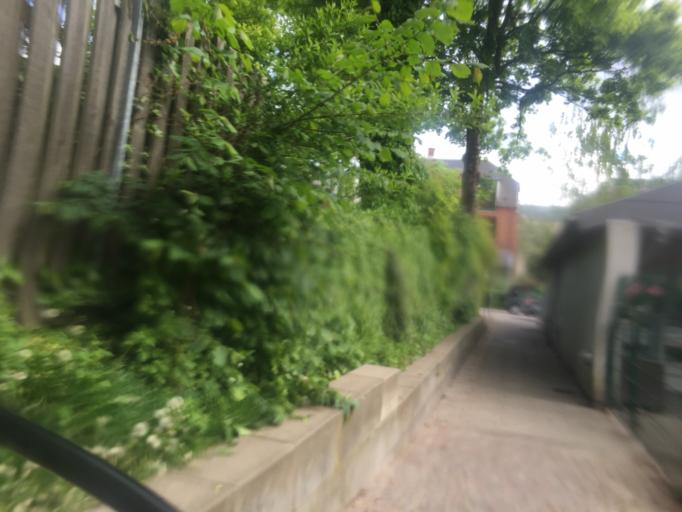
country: DK
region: Capital Region
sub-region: Frederiksberg Kommune
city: Frederiksberg
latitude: 55.6768
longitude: 12.5346
